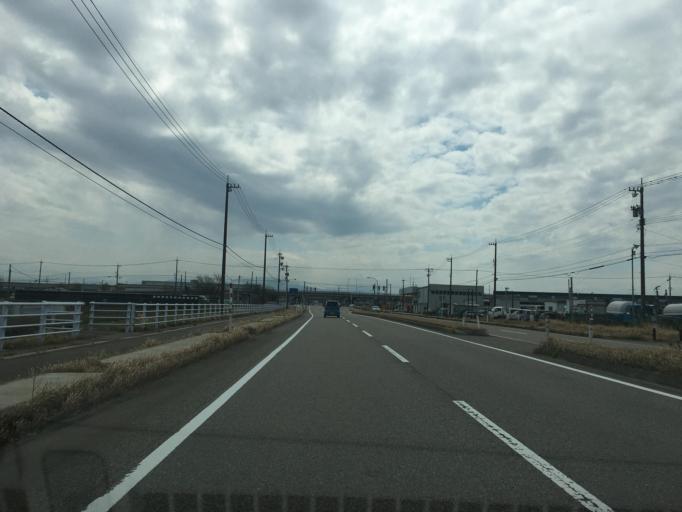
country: JP
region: Toyama
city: Kuragaki-kosugi
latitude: 36.7325
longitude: 137.1260
